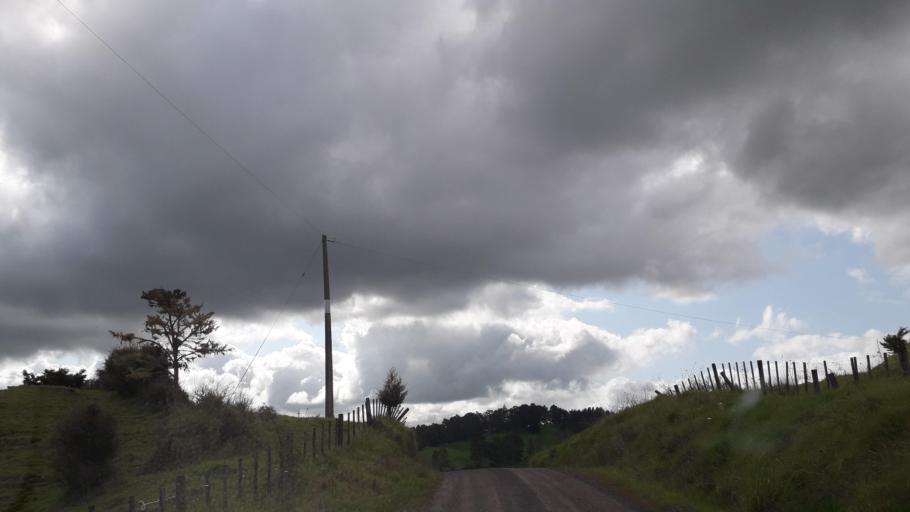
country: NZ
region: Northland
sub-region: Far North District
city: Waimate North
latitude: -35.3122
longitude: 173.5651
